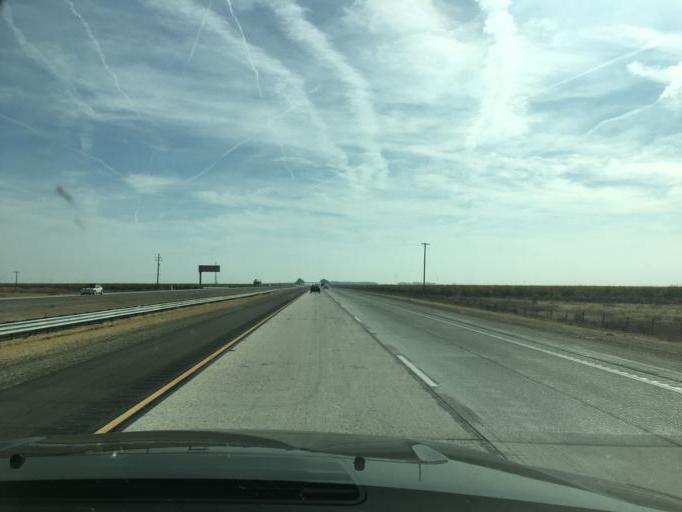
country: US
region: California
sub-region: Kern County
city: Lost Hills
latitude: 35.5884
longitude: -119.6290
